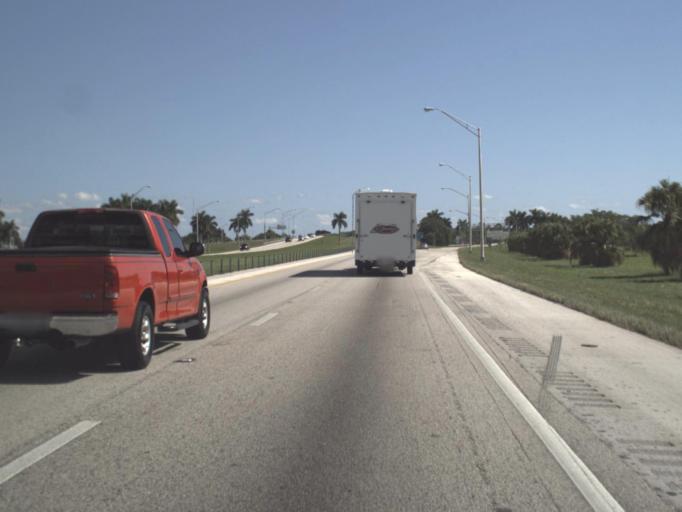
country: US
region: Florida
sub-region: Miami-Dade County
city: Goulds
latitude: 25.5311
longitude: -80.3779
